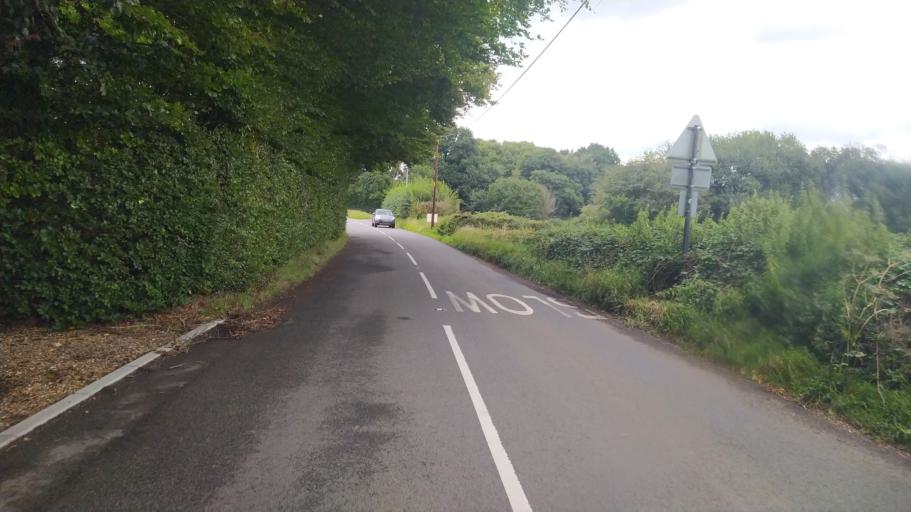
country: GB
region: England
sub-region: Dorset
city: Verwood
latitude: 50.9117
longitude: -1.8951
